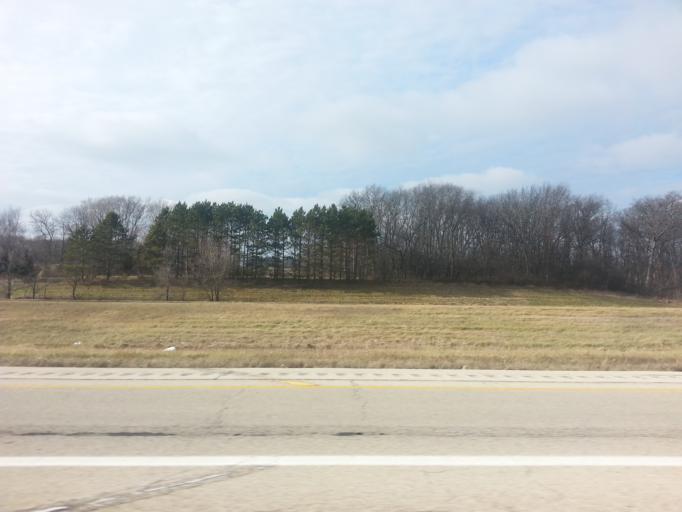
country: US
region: Illinois
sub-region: Winnebago County
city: Cherry Valley
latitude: 42.2092
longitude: -89.0115
